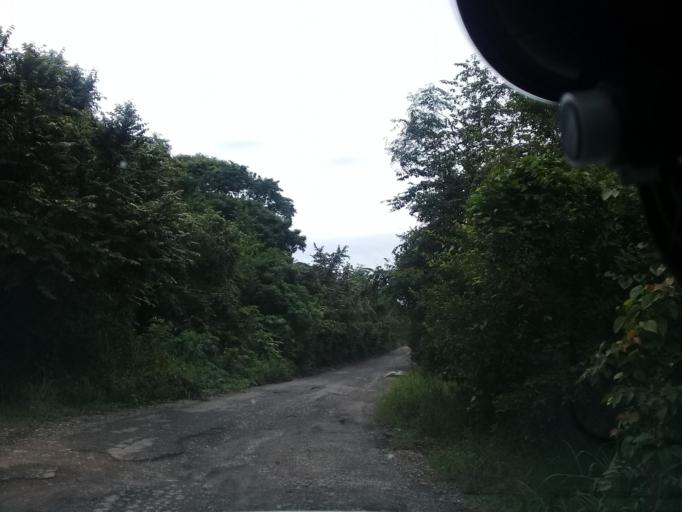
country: MX
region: Hidalgo
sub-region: Huejutla de Reyes
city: Chalahuiyapa
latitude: 21.2011
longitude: -98.3509
